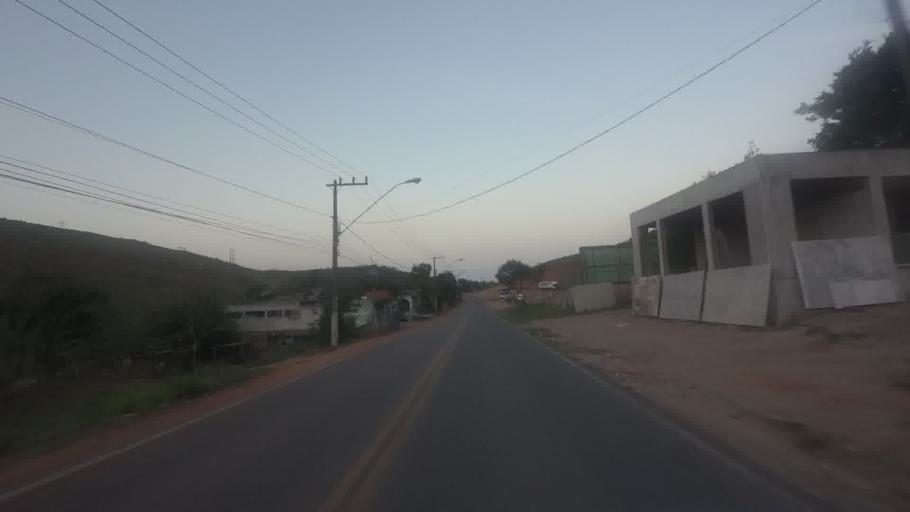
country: BR
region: Espirito Santo
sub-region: Piuma
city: Piuma
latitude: -20.8877
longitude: -40.7693
